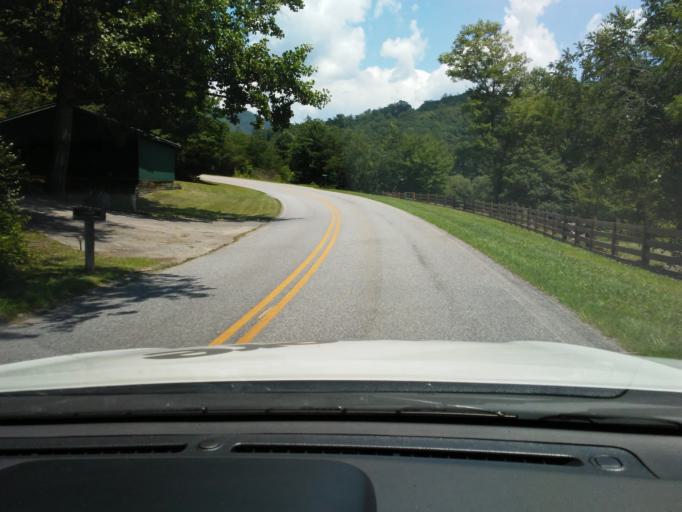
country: US
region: Georgia
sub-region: Towns County
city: Hiawassee
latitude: 34.8668
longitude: -83.7370
